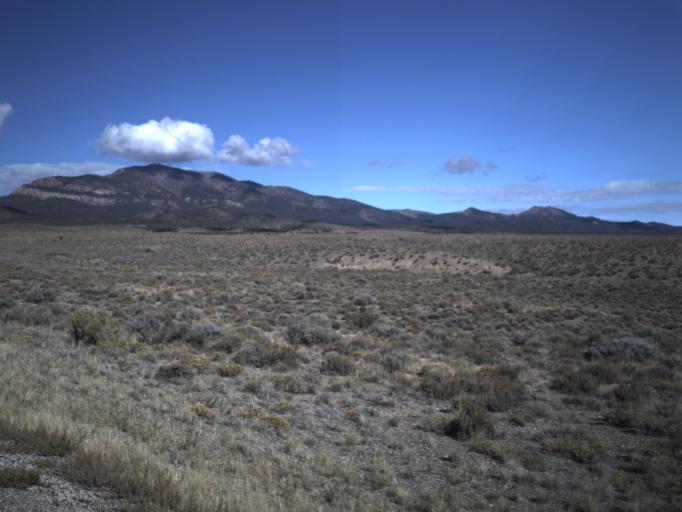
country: US
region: Utah
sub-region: Beaver County
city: Milford
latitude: 38.4534
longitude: -113.2082
